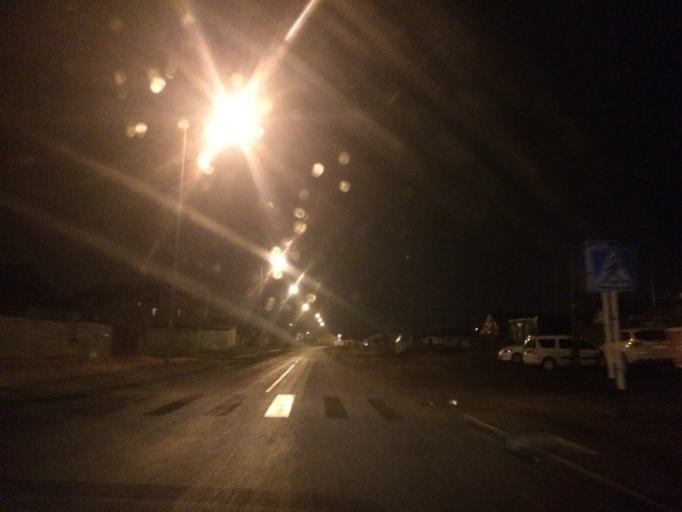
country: KZ
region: Astana Qalasy
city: Astana
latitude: 51.1939
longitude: 71.3856
